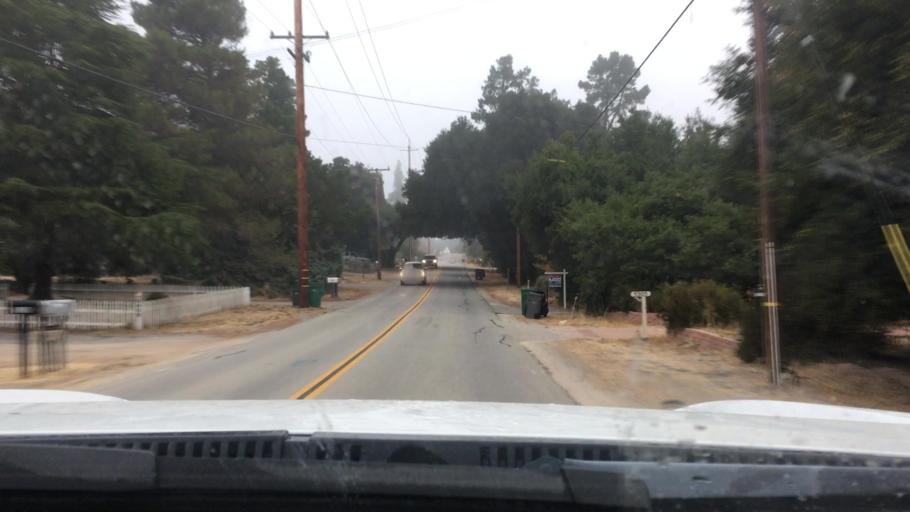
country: US
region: California
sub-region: San Luis Obispo County
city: Atascadero
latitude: 35.4857
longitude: -120.6850
